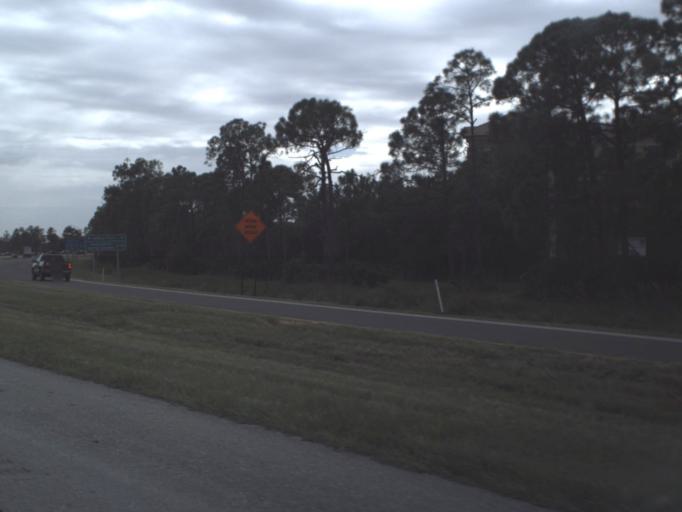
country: US
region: Florida
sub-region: Lee County
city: Gateway
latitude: 26.5509
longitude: -81.7952
